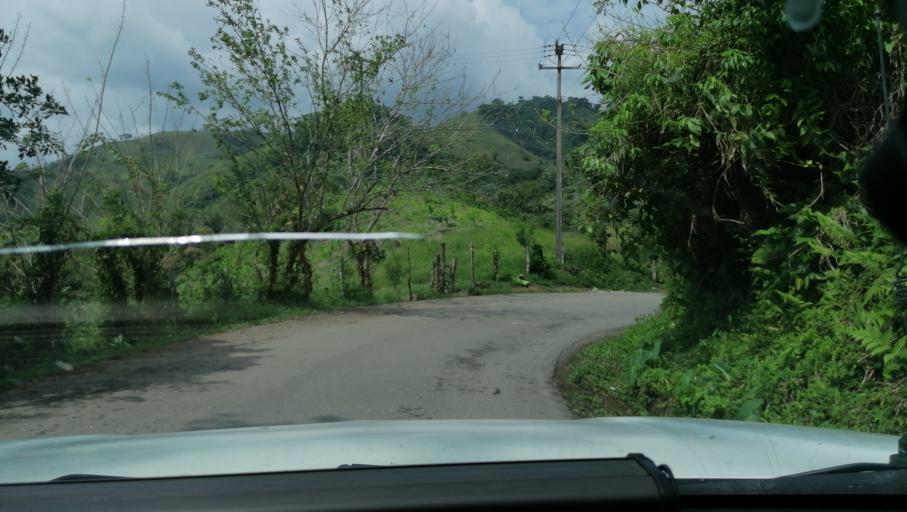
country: MX
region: Chiapas
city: Ocotepec
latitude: 17.3228
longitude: -93.1683
